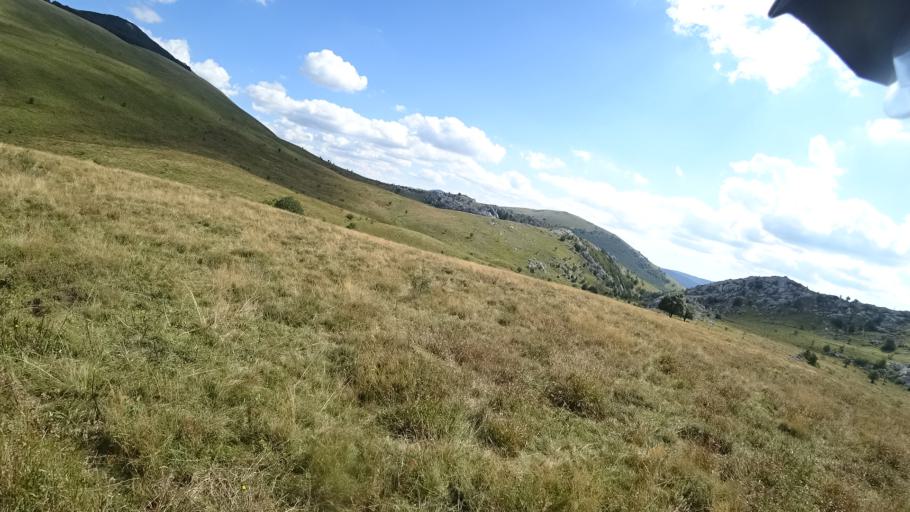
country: HR
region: Zadarska
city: Gracac
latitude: 44.4128
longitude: 16.0001
